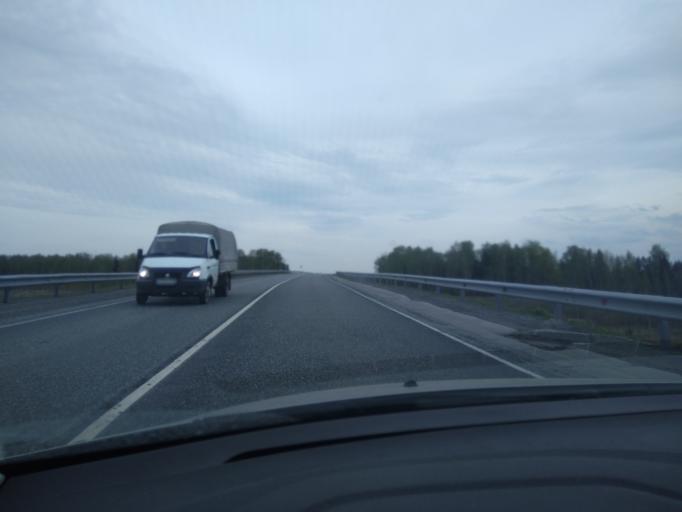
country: RU
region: Sverdlovsk
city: Kamyshlov
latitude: 56.8580
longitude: 62.8043
